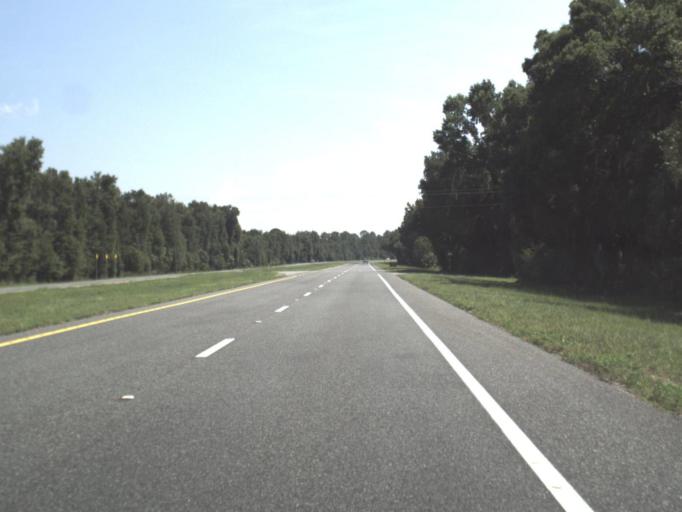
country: US
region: Florida
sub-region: Levy County
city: Inglis
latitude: 29.0979
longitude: -82.6362
